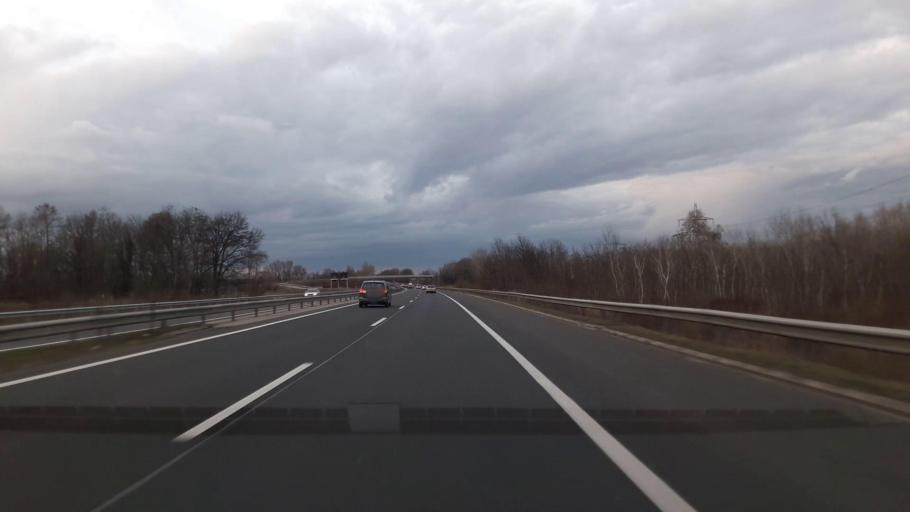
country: AT
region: Burgenland
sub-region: Eisenstadt-Umgebung
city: Wimpassing an der Leitha
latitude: 47.9027
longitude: 16.4131
